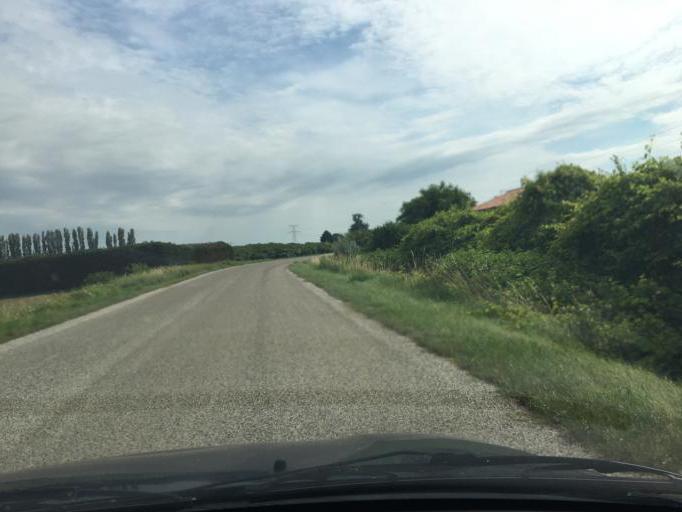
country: FR
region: Rhone-Alpes
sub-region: Departement de la Drome
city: Clerieux
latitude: 45.1165
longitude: 4.9400
